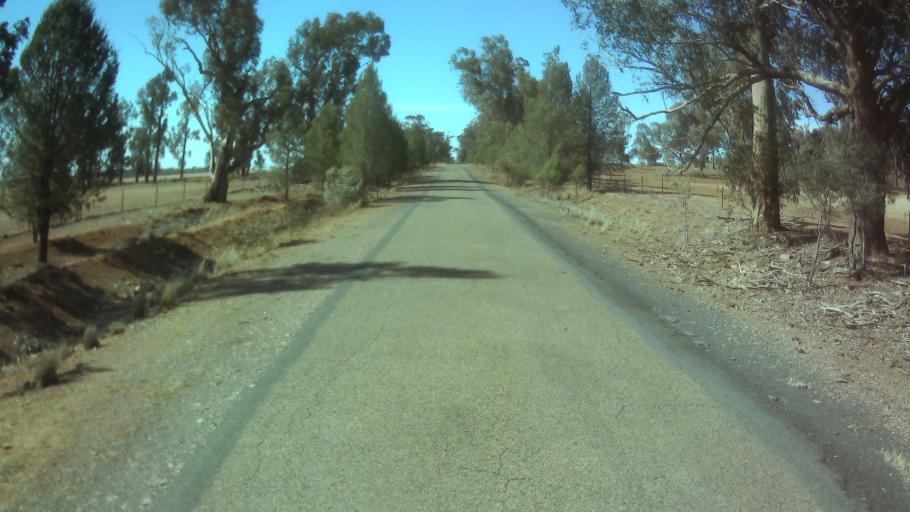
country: AU
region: New South Wales
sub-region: Forbes
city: Forbes
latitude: -33.7331
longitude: 147.7425
